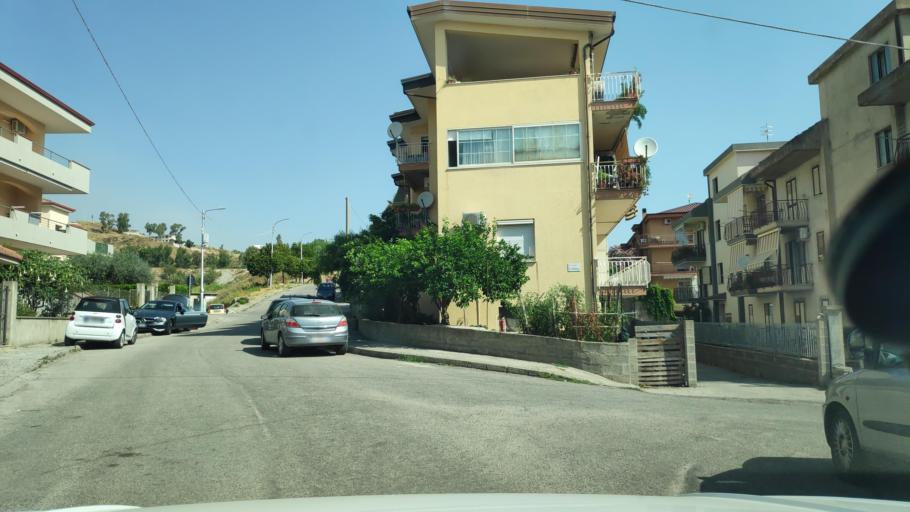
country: IT
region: Calabria
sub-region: Provincia di Catanzaro
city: Santa Caterina dello Ionio Marina
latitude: 38.5288
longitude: 16.5692
